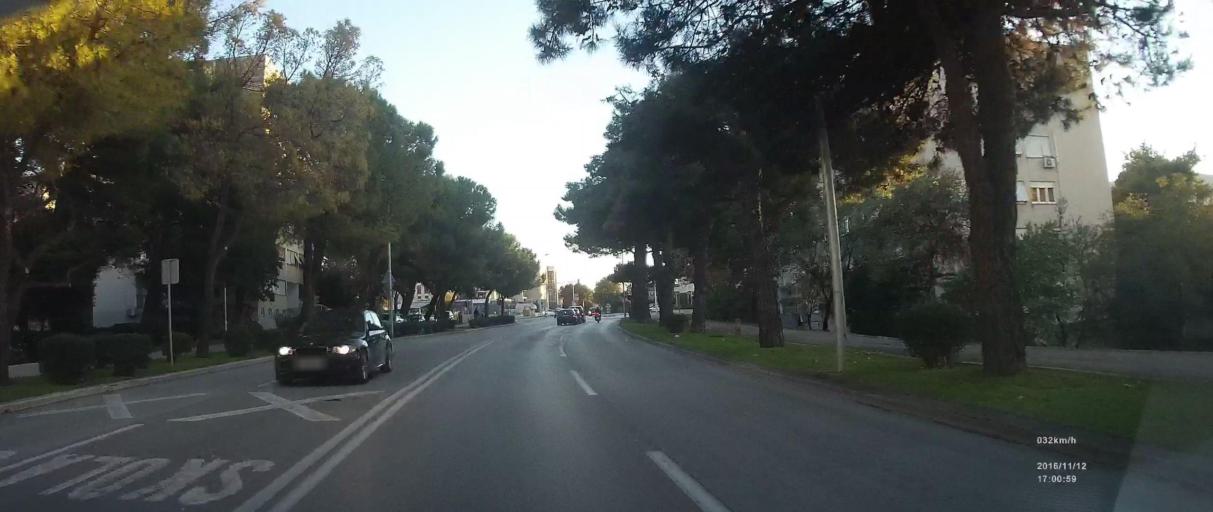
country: HR
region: Splitsko-Dalmatinska
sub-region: Grad Split
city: Split
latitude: 43.5140
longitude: 16.4492
